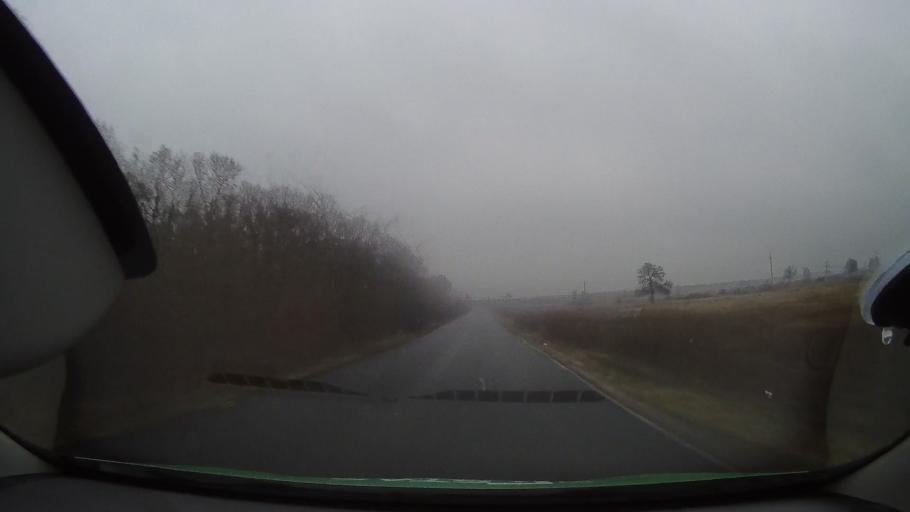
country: RO
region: Bihor
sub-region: Comuna Tinca
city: Gurbediu
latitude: 46.7768
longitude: 21.8789
